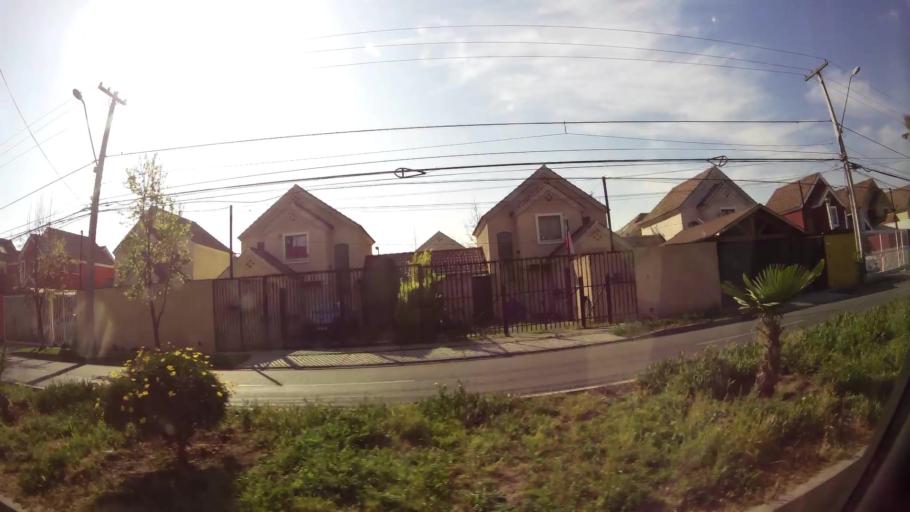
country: CL
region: Santiago Metropolitan
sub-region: Provincia de Santiago
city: Lo Prado
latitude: -33.4505
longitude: -70.7631
